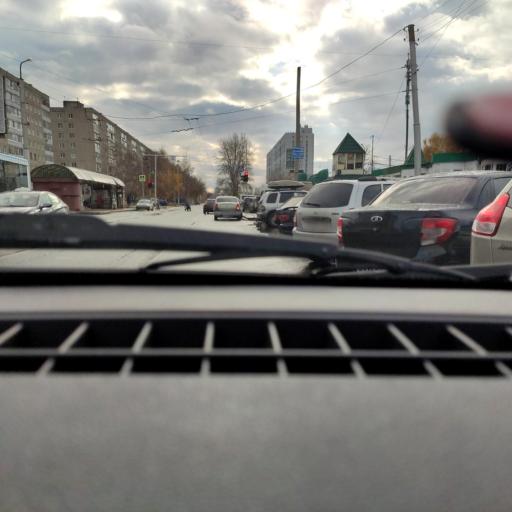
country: RU
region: Bashkortostan
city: Ufa
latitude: 54.7793
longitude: 56.1243
